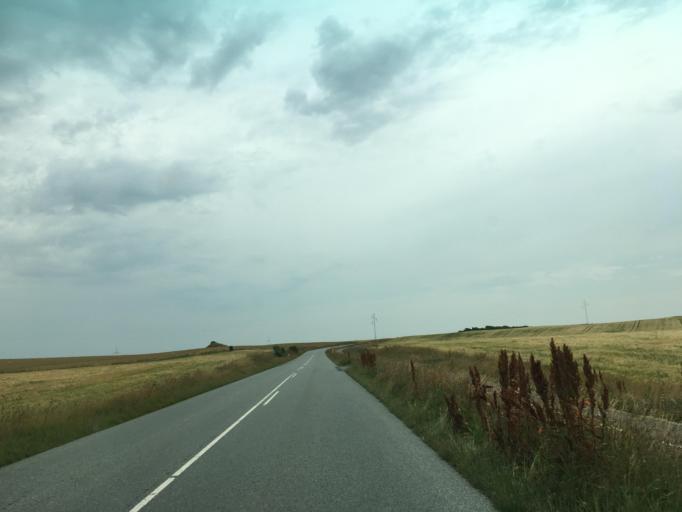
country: DK
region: North Denmark
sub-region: Thisted Kommune
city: Hurup
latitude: 56.7808
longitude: 8.4192
